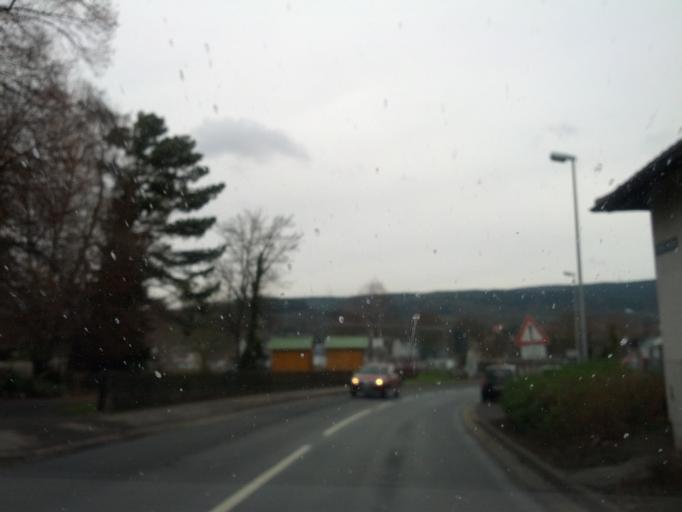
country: DE
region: Hesse
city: Witzenhausen
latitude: 51.3424
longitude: 9.8535
